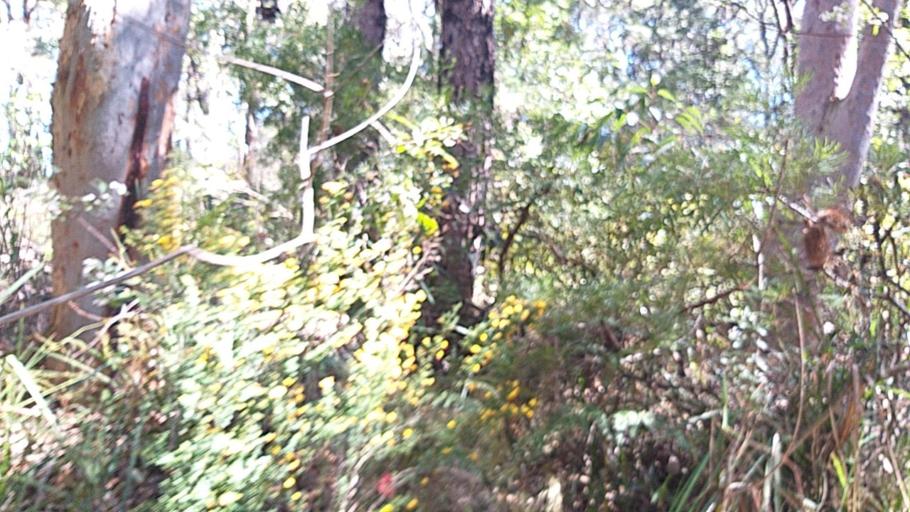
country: AU
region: New South Wales
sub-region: Ryde
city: East Ryde
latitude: -33.8157
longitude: 151.1283
